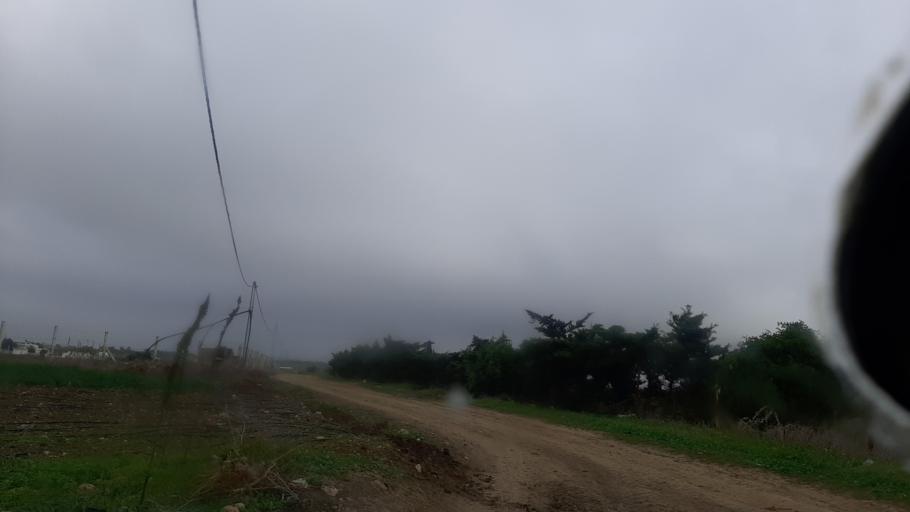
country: TN
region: Nabul
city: Qulaybiyah
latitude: 36.8324
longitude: 11.0346
